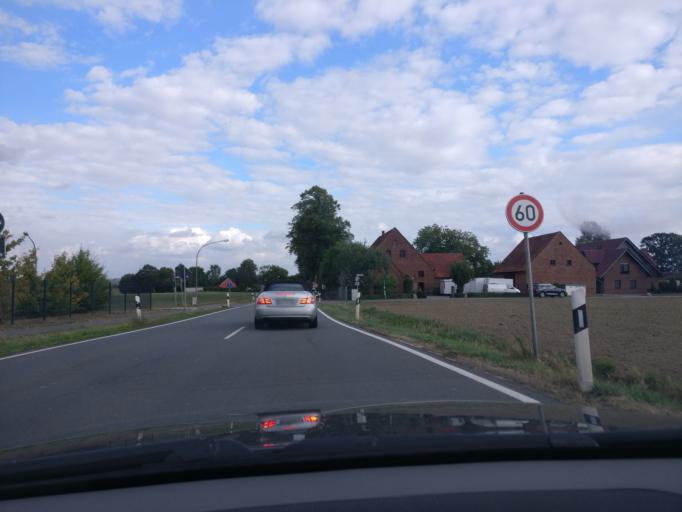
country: DE
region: Lower Saxony
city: Melle
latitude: 52.1892
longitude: 8.3560
